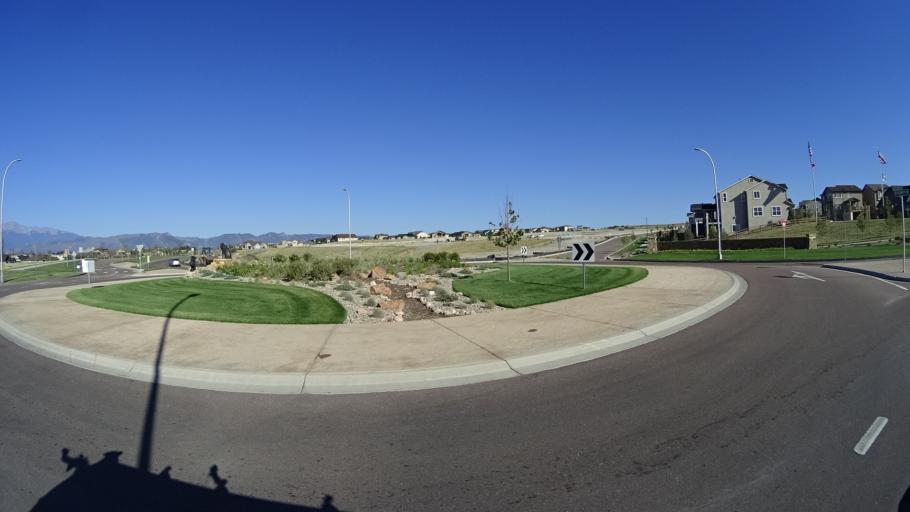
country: US
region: Colorado
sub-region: El Paso County
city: Black Forest
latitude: 38.9709
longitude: -104.7241
